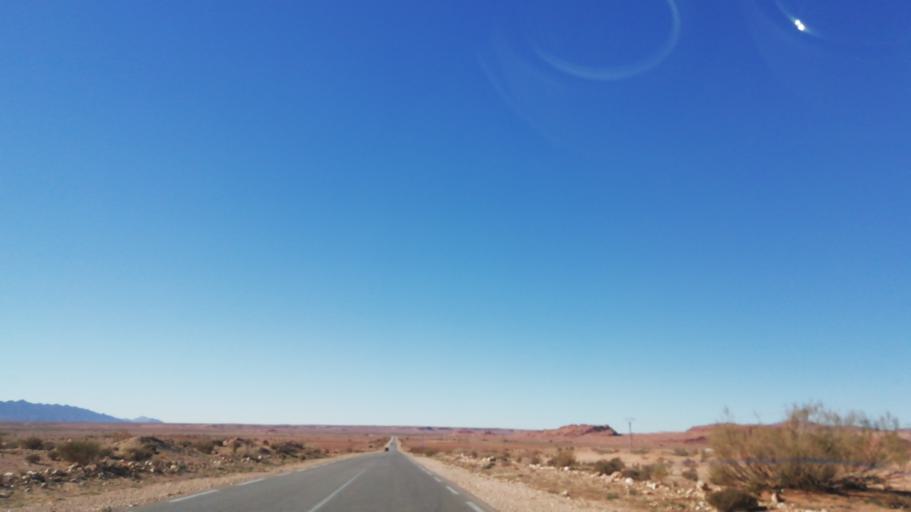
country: DZ
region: El Bayadh
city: El Abiodh Sidi Cheikh
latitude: 33.1792
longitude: 0.5411
